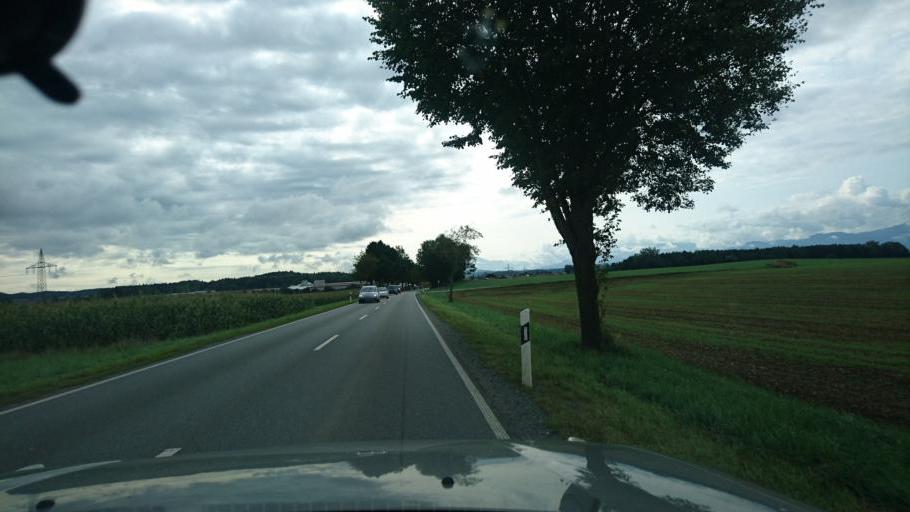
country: DE
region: Bavaria
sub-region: Upper Bavaria
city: Chieming
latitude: 47.9132
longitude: 12.5255
